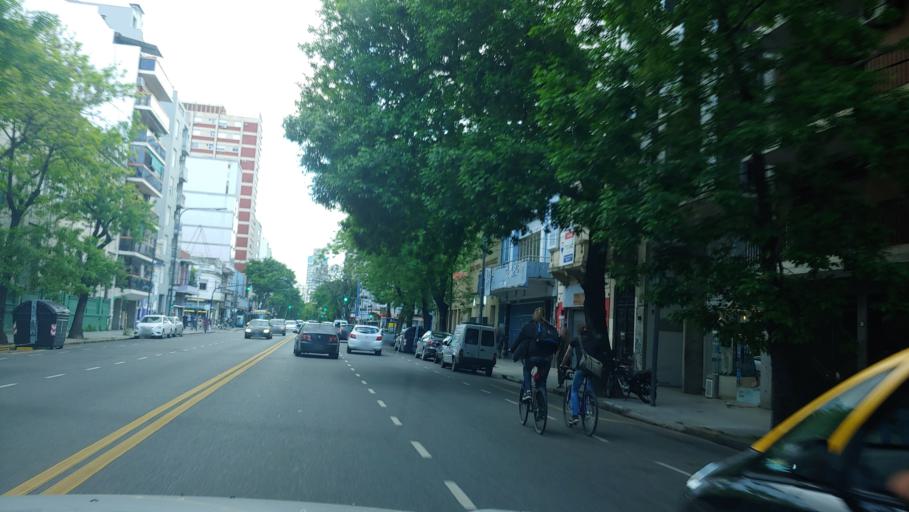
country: AR
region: Buenos Aires F.D.
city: Colegiales
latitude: -34.5751
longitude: -58.4479
